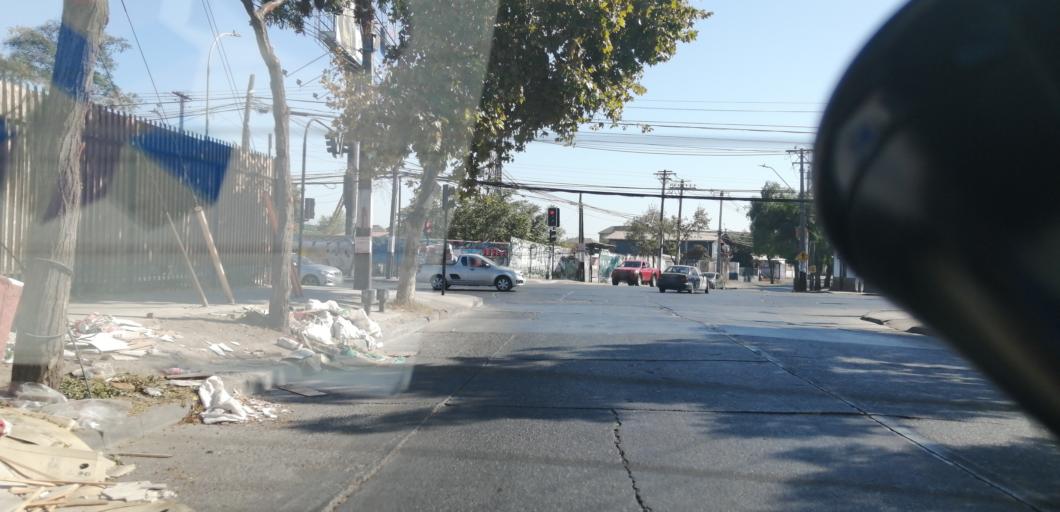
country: CL
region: Santiago Metropolitan
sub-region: Provincia de Santiago
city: Lo Prado
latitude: -33.4432
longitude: -70.7690
